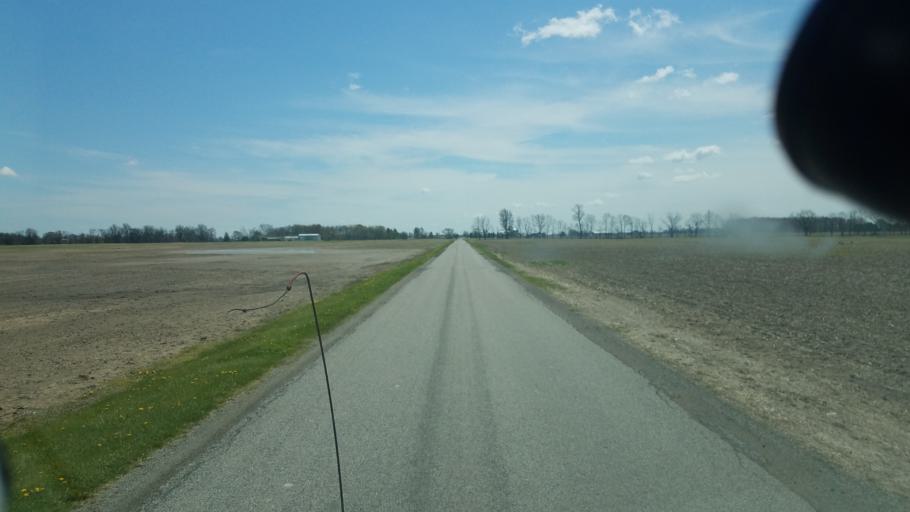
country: US
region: Ohio
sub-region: Union County
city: Richwood
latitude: 40.4596
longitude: -83.2504
